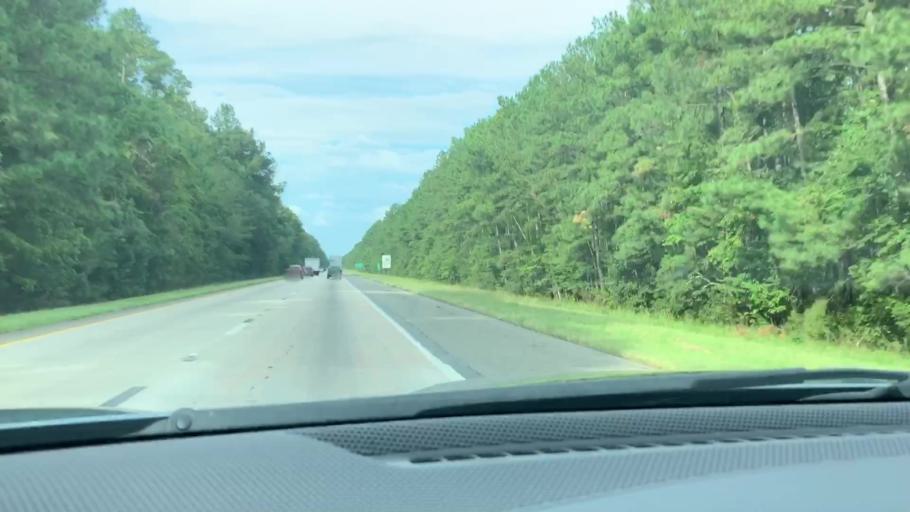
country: US
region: South Carolina
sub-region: Colleton County
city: Walterboro
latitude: 32.9800
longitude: -80.6739
